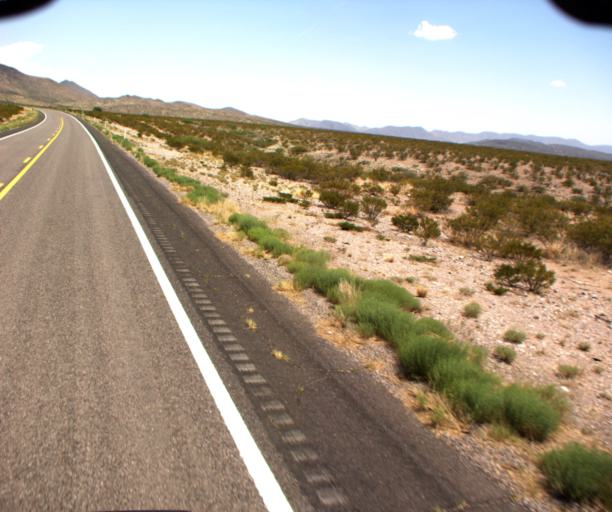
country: US
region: Arizona
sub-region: Greenlee County
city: Clifton
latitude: 32.7519
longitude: -109.3483
